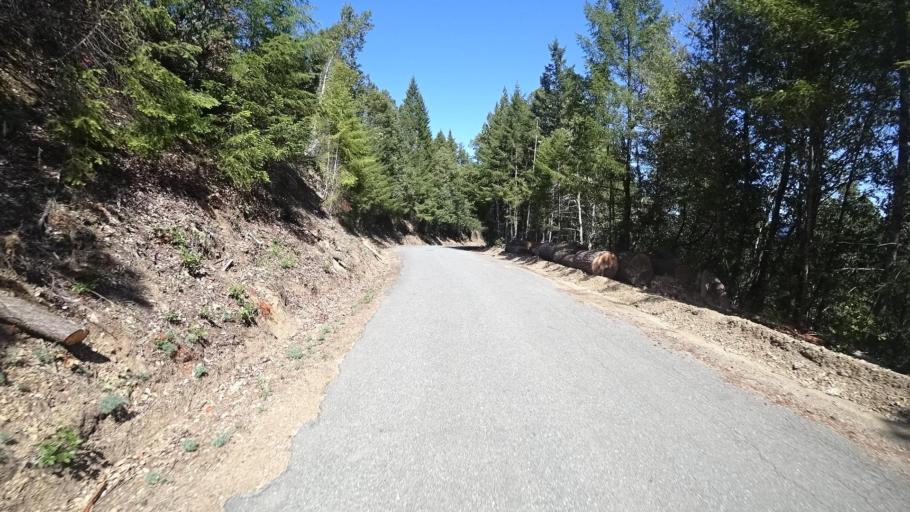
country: US
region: California
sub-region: Humboldt County
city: Redway
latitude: 40.1525
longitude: -124.0653
